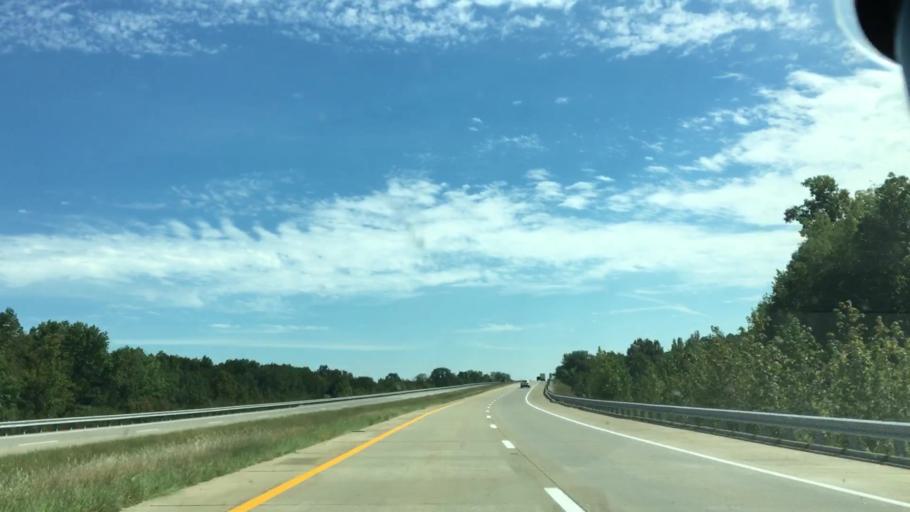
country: US
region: Kentucky
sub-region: Daviess County
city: Owensboro
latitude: 37.7603
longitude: -87.3015
